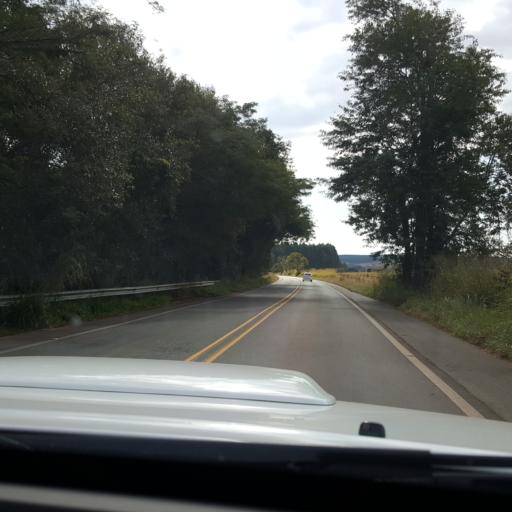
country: BR
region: Sao Paulo
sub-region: Itaporanga
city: Itaporanga
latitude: -23.7275
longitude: -49.4601
